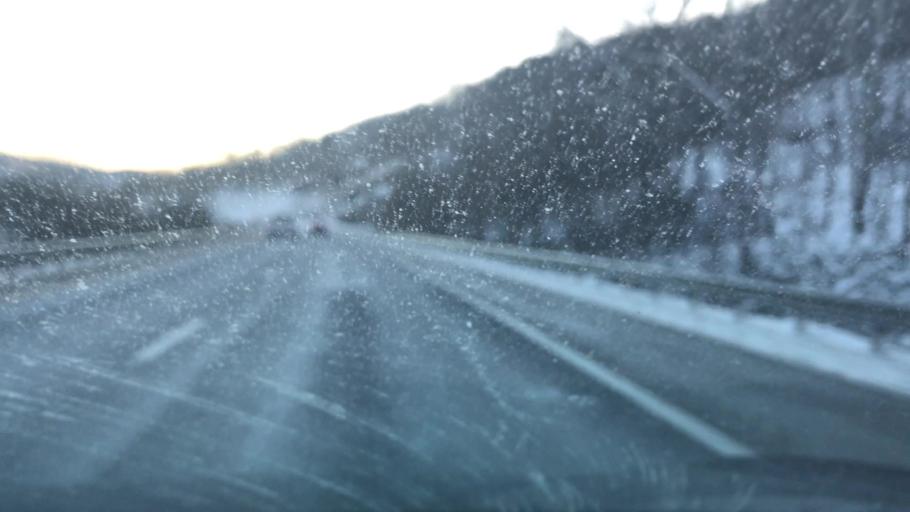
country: US
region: Virginia
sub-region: Montgomery County
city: Shawsville
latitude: 37.2267
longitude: -80.2472
